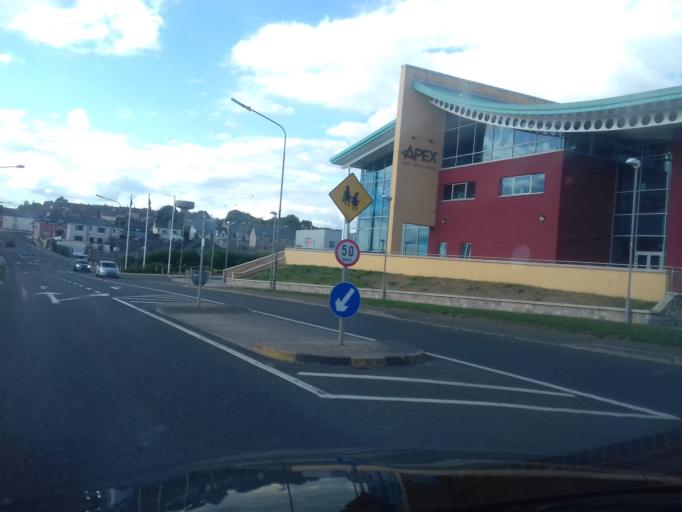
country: IE
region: Leinster
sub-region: Loch Garman
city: New Ross
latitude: 52.3965
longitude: -6.9348
